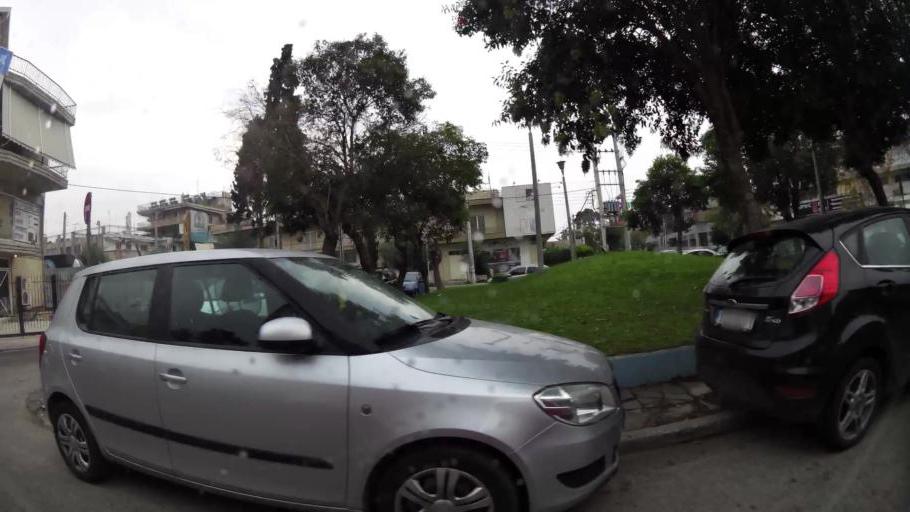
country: GR
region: Attica
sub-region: Nomarchia Athinas
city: Peristeri
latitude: 38.0058
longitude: 23.7070
